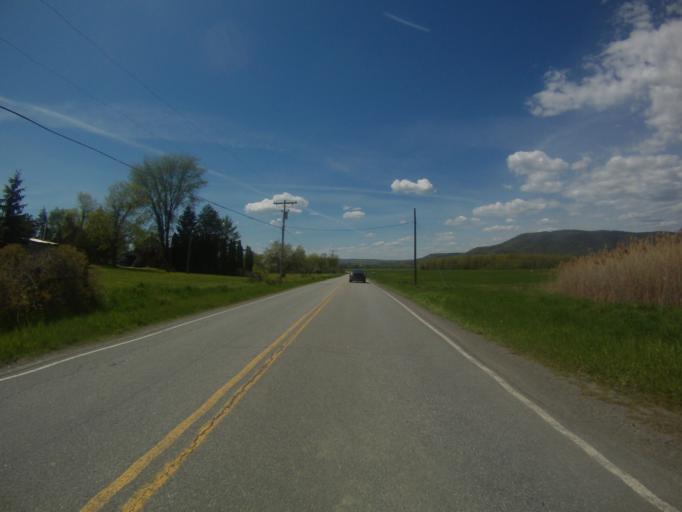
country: US
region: New York
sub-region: Essex County
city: Port Henry
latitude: 43.9984
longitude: -73.4175
